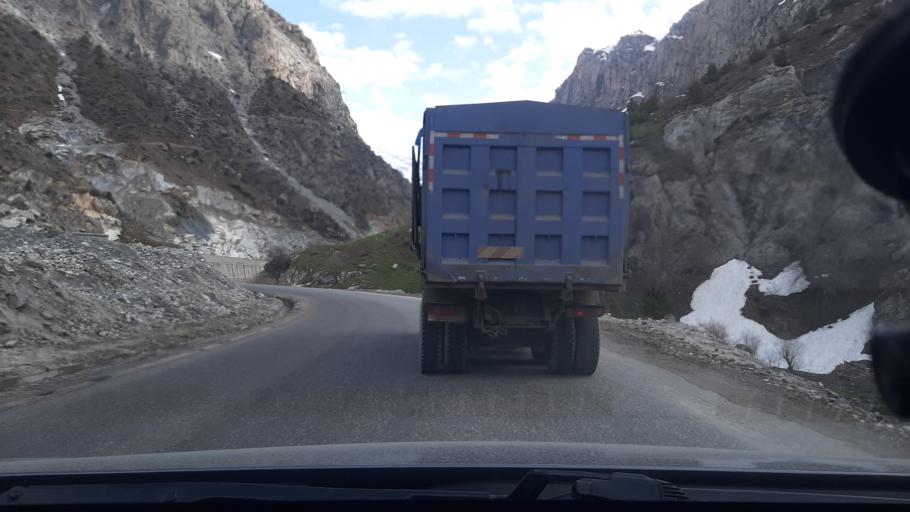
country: TJ
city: Tagob
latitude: 39.0013
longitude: 68.7713
